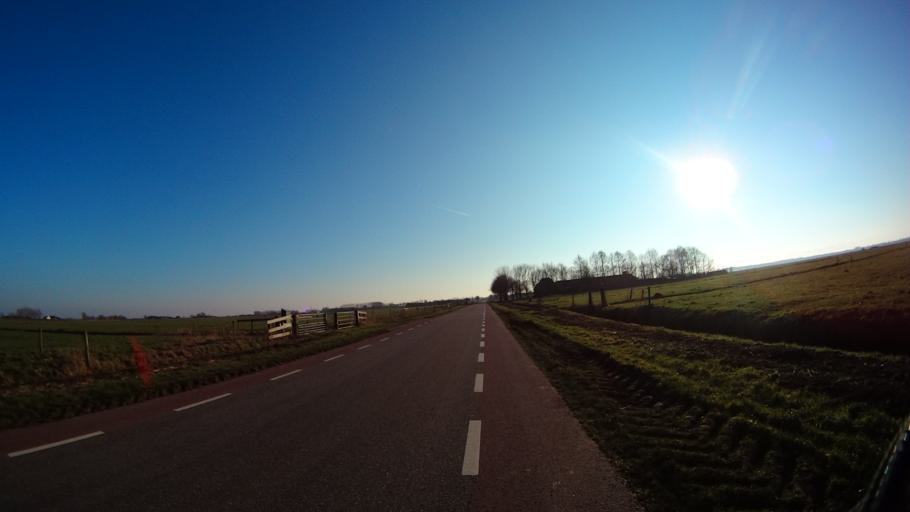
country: NL
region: Utrecht
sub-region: Gemeente Baarn
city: Baarn
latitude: 52.2420
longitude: 5.3019
